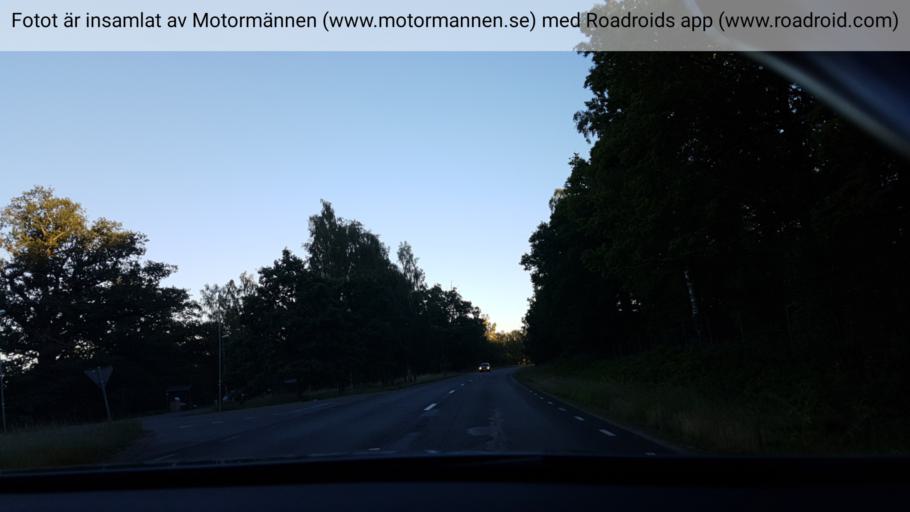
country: SE
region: Vaestra Goetaland
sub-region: Hjo Kommun
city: Hjo
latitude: 58.3570
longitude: 14.3527
